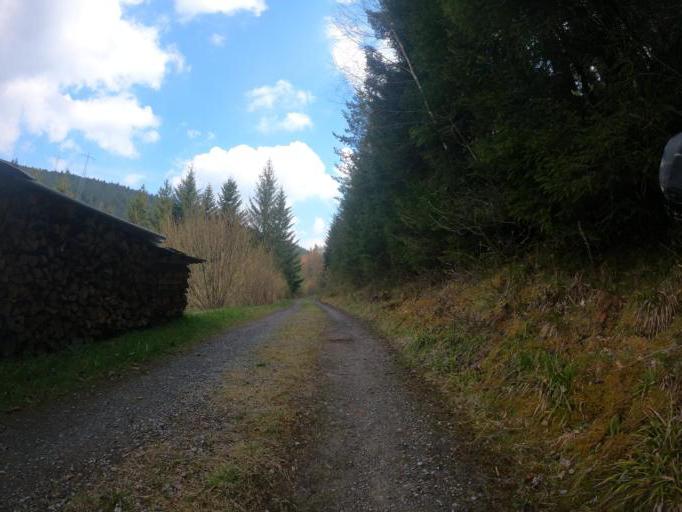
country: DE
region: Baden-Wuerttemberg
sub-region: Karlsruhe Region
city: Hofen an der Enz
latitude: 48.7724
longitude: 8.5989
